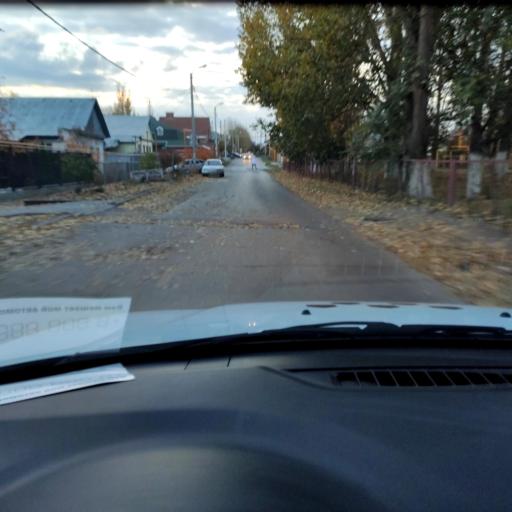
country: RU
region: Samara
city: Tol'yatti
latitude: 53.5268
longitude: 49.4018
